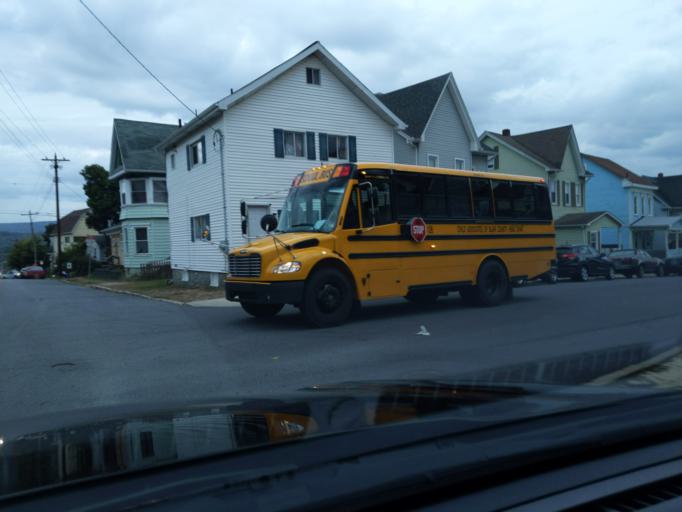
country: US
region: Pennsylvania
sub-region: Blair County
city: Altoona
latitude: 40.5116
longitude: -78.3902
